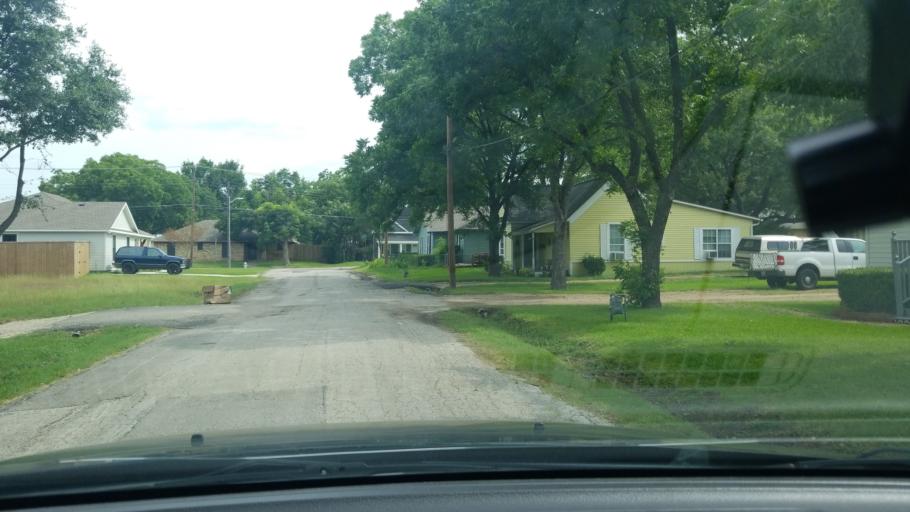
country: US
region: Texas
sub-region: Dallas County
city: Mesquite
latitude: 32.7678
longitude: -96.5965
